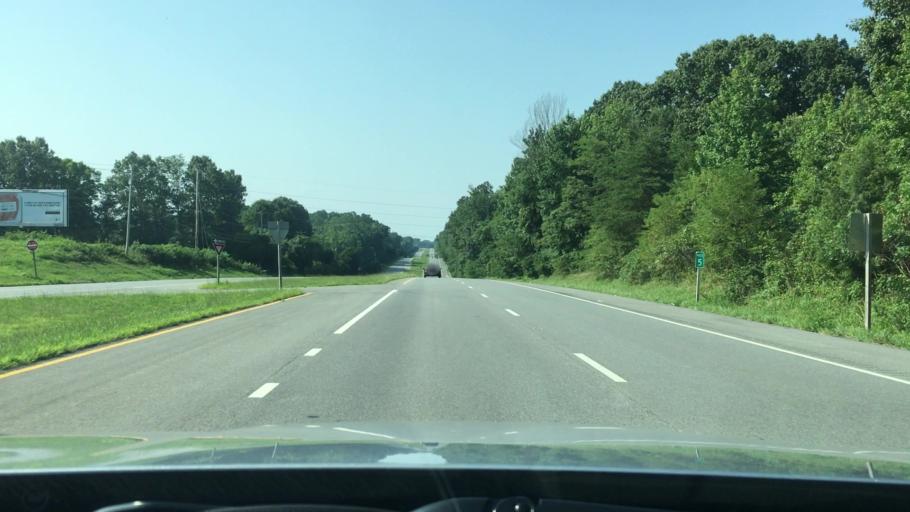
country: US
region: Virginia
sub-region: King George County
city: Dahlgren
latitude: 38.3984
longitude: -76.9534
